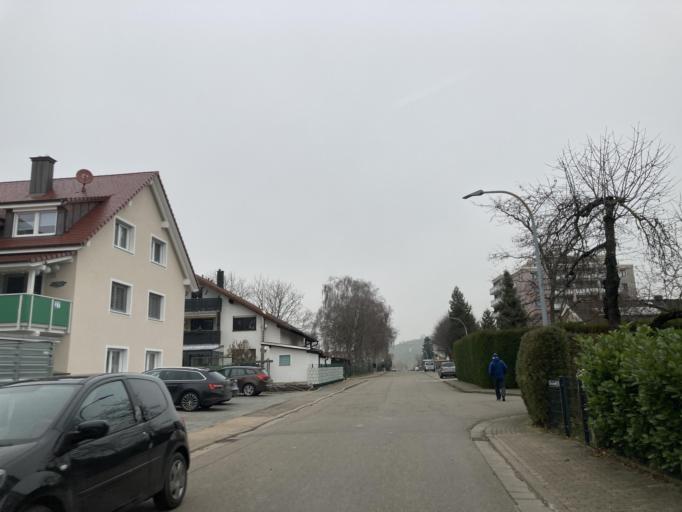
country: DE
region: Baden-Wuerttemberg
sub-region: Freiburg Region
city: Auggen
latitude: 47.7898
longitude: 7.5944
